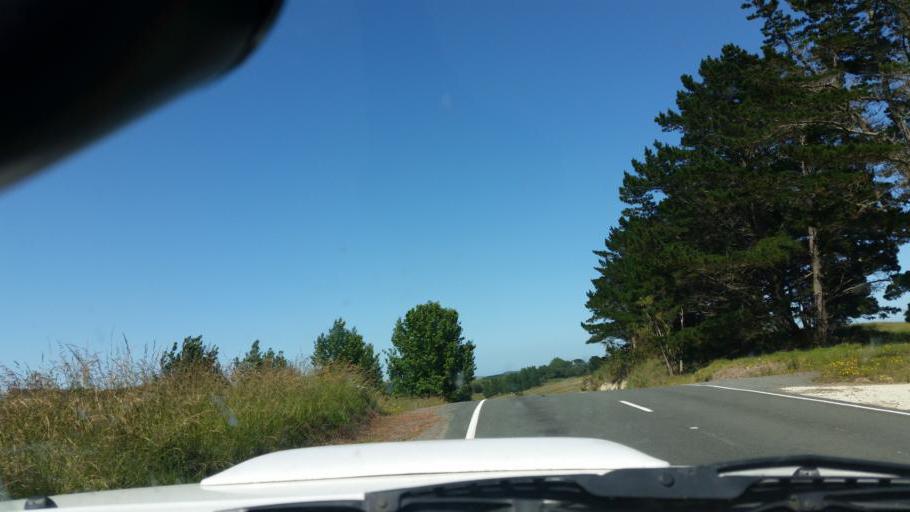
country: NZ
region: Auckland
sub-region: Auckland
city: Wellsford
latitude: -36.2232
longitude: 174.3786
